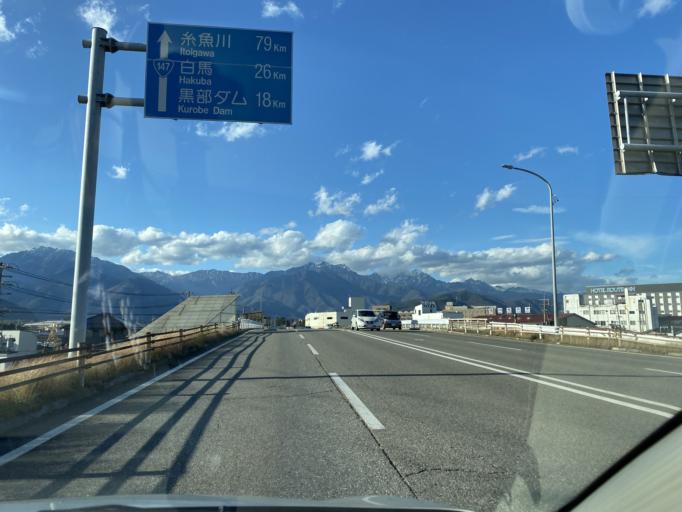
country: JP
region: Nagano
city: Omachi
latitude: 36.4976
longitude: 137.8608
